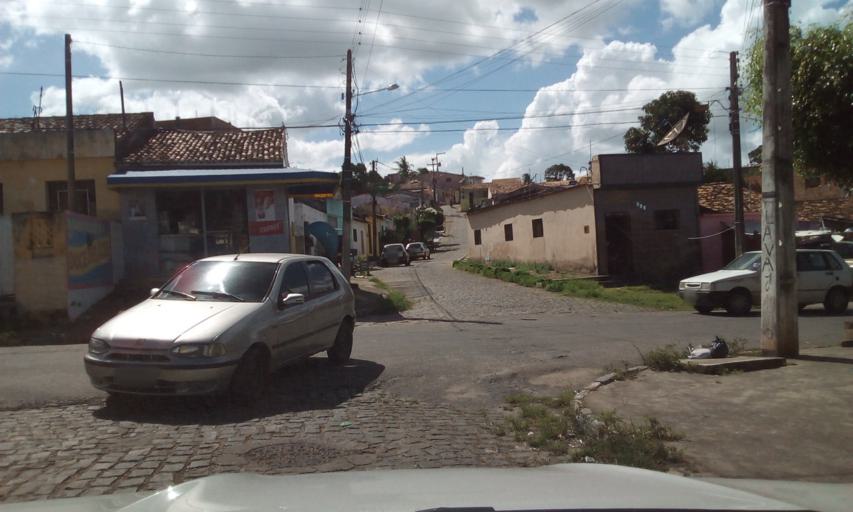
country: BR
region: Paraiba
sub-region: Guarabira
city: Guarabira
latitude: -6.8545
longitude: -35.4815
